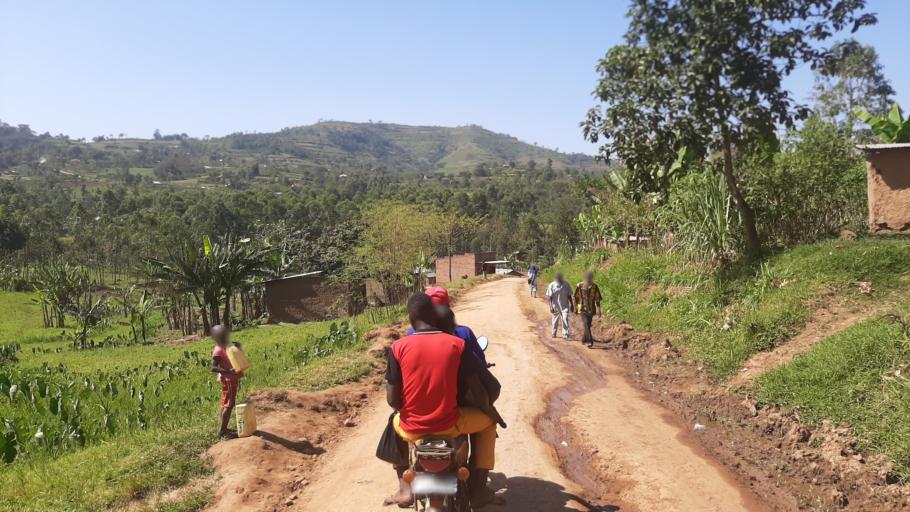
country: UG
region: Eastern Region
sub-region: Manafwa District
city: Manafwa
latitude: 0.9108
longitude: 34.3286
